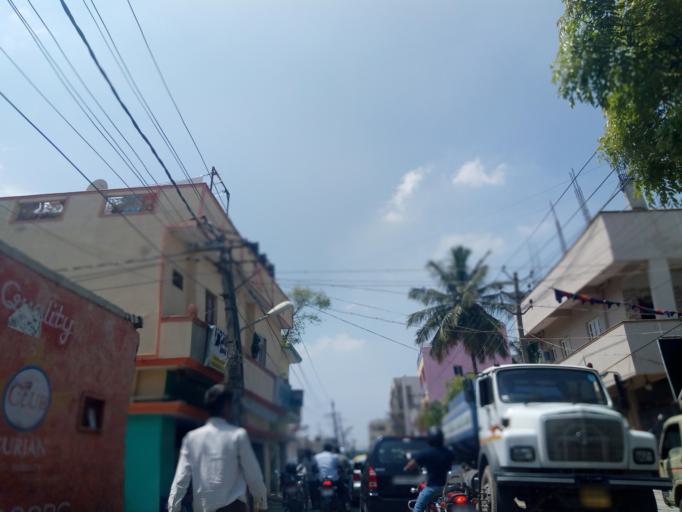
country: IN
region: Karnataka
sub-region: Bangalore Urban
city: Bangalore
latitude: 12.8971
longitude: 77.6511
